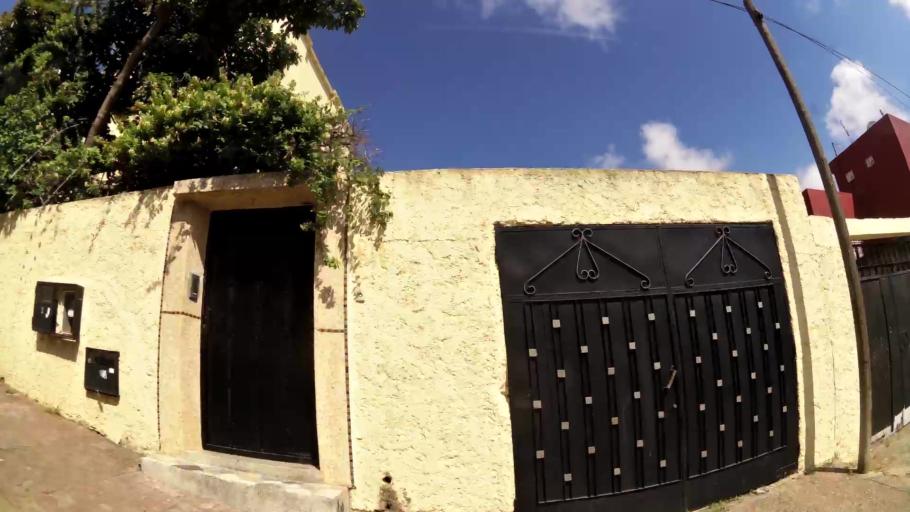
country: MA
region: Rabat-Sale-Zemmour-Zaer
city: Sale
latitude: 34.0389
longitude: -6.7921
